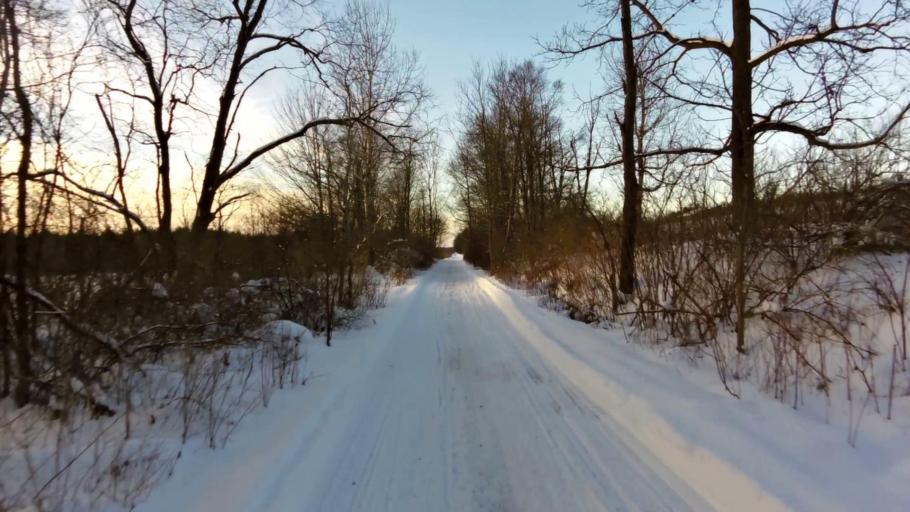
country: US
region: New York
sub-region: Chautauqua County
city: Celoron
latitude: 42.1979
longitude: -79.2554
